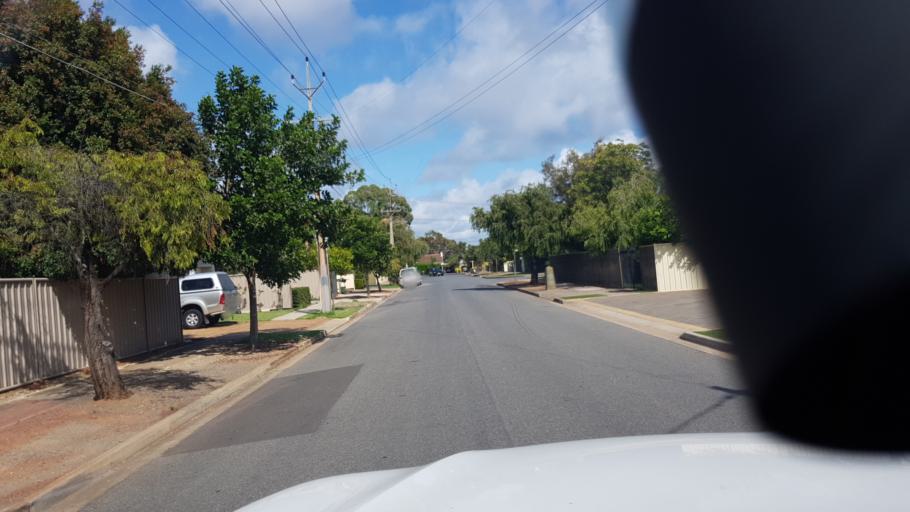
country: AU
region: South Australia
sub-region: Holdfast Bay
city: Seacliff Park
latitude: -35.0224
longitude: 138.5338
